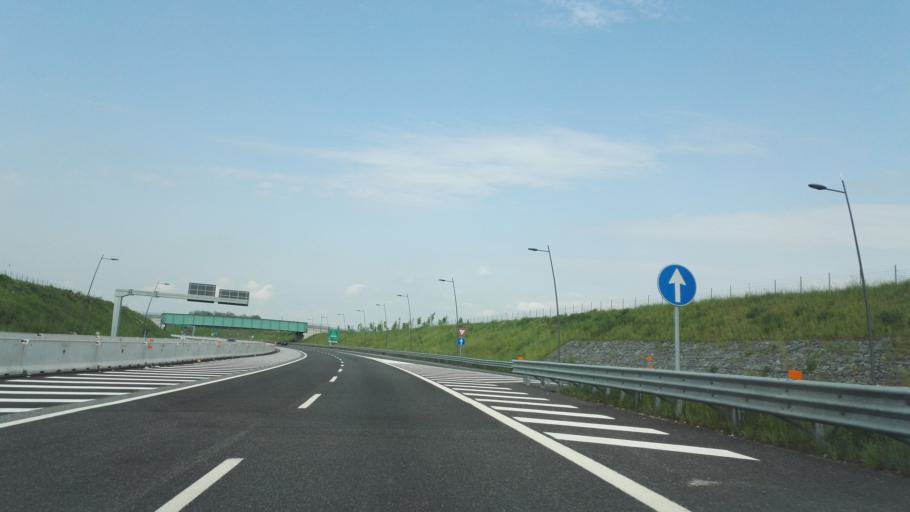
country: IT
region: Lombardy
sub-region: Provincia di Monza e Brianza
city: Lazzate
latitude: 45.6859
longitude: 9.0870
